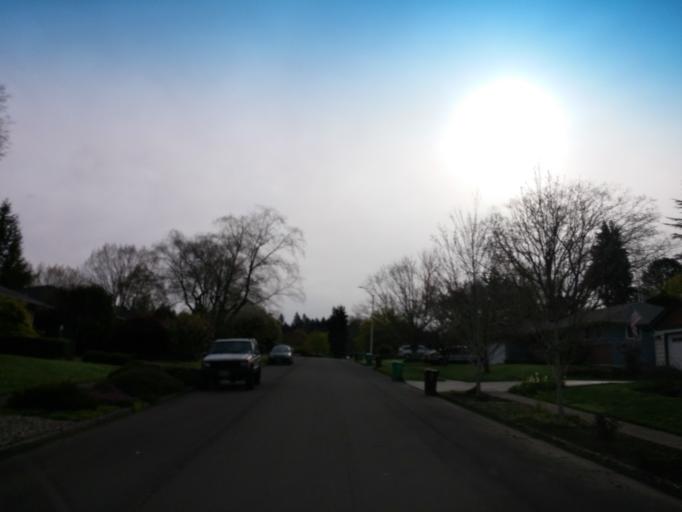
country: US
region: Oregon
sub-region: Washington County
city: Cedar Hills
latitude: 45.5099
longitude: -122.8021
